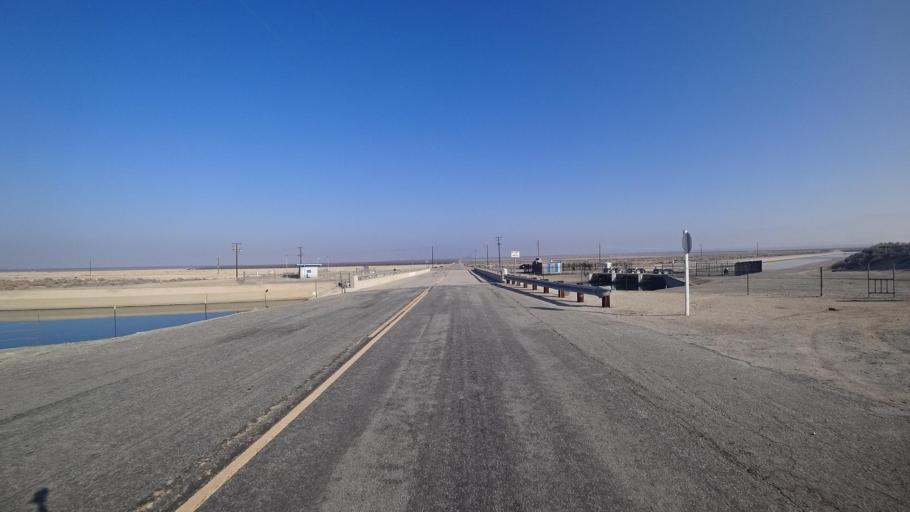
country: US
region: California
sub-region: Kern County
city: Maricopa
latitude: 35.1012
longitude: -119.3695
